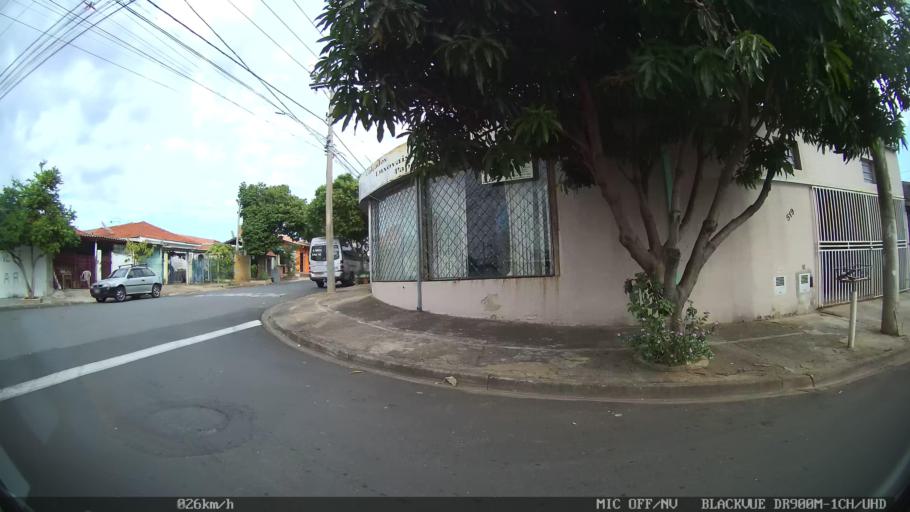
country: BR
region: Sao Paulo
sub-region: Americana
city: Americana
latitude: -22.7198
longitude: -47.3591
